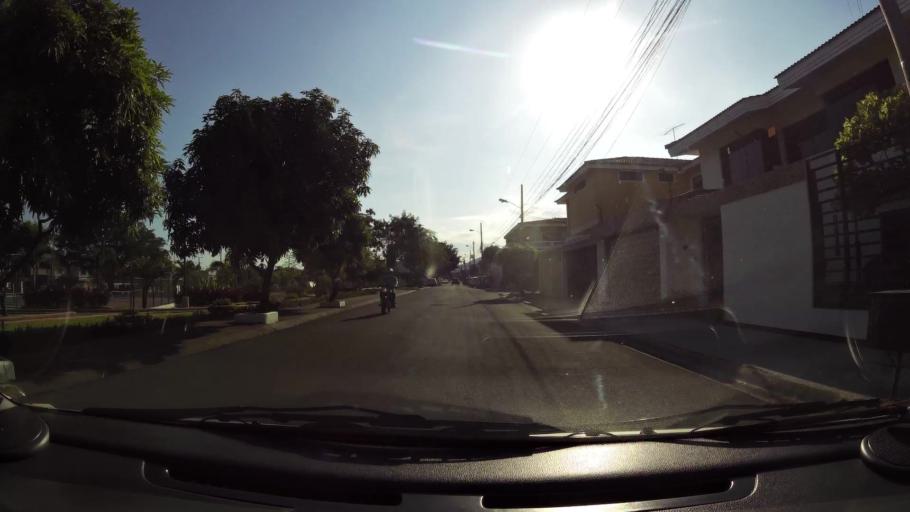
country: EC
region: Guayas
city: Santa Lucia
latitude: -2.1869
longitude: -79.9690
